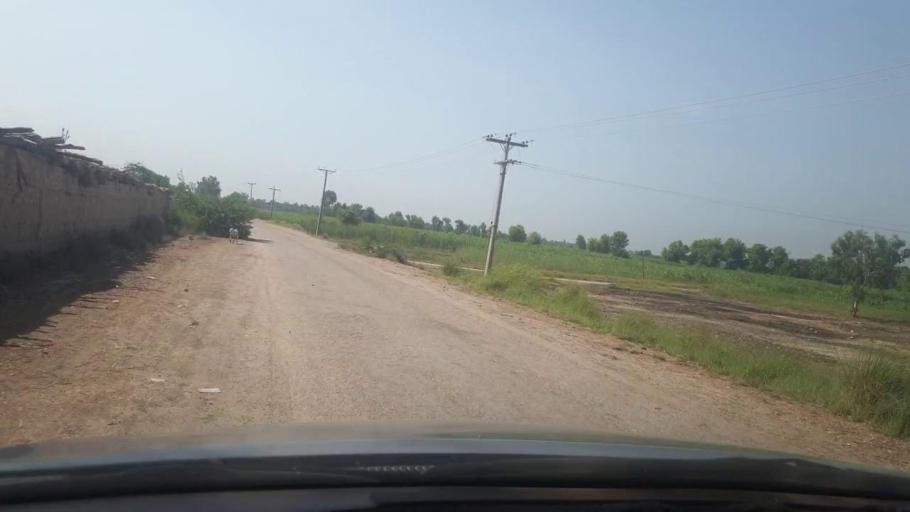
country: PK
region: Sindh
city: Ranipur
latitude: 27.2928
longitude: 68.5743
